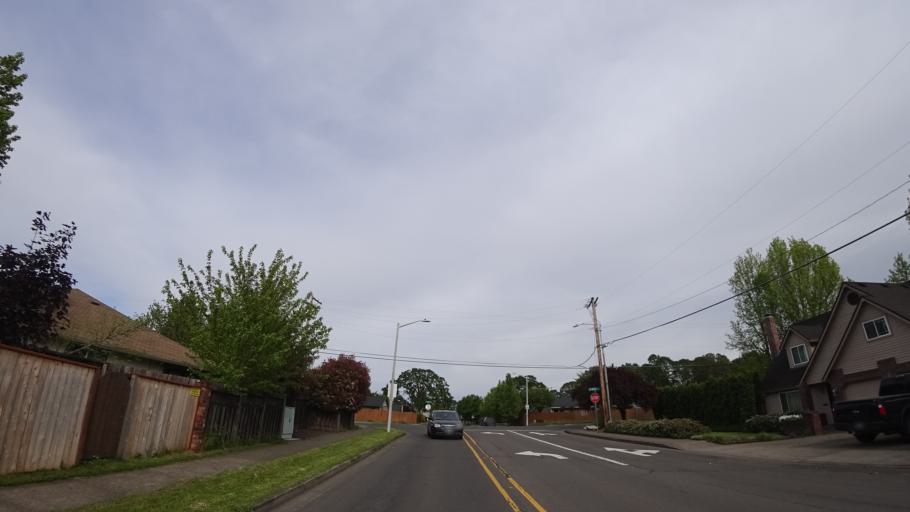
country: US
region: Oregon
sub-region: Washington County
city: Aloha
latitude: 45.5077
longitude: -122.9232
